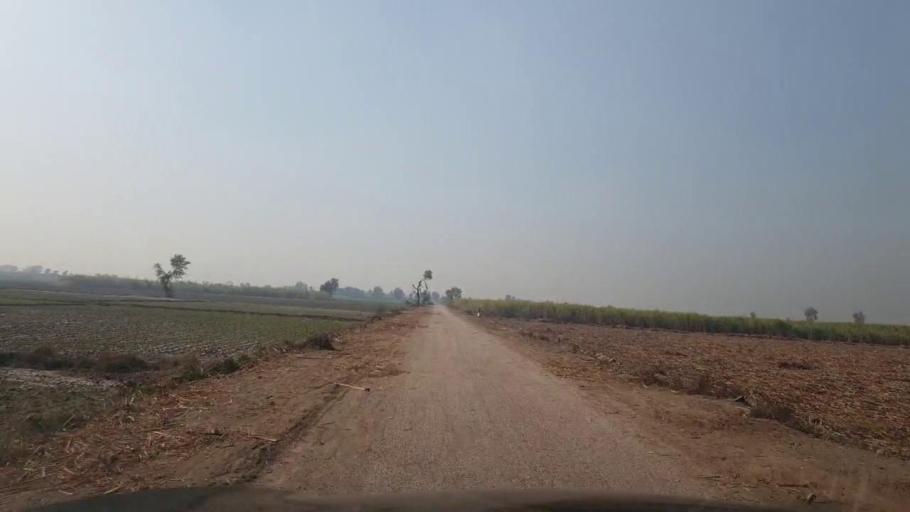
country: PK
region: Sindh
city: Ubauro
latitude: 28.1234
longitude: 69.8180
